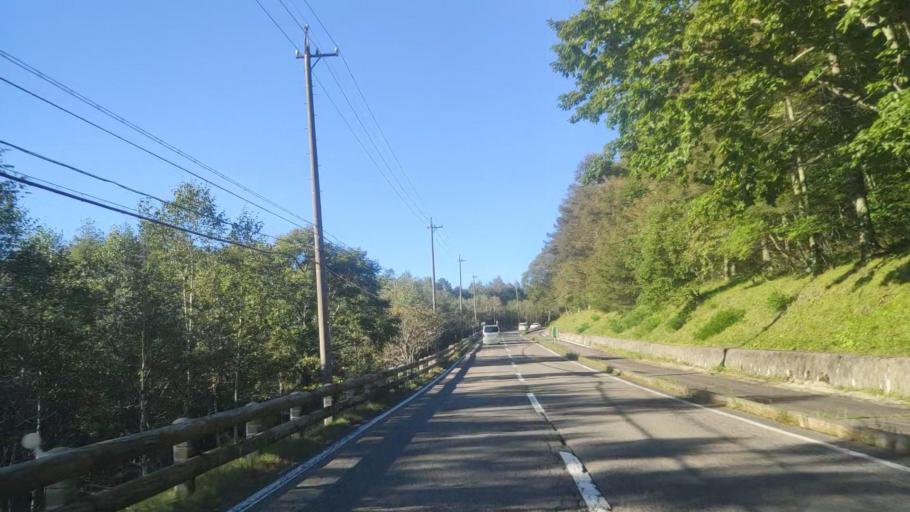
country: JP
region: Nagano
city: Kamimaruko
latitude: 36.1429
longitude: 138.2719
